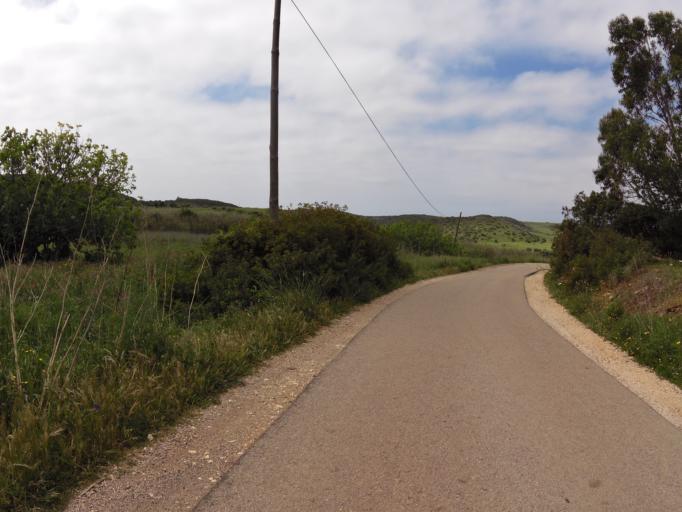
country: PT
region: Faro
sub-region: Vila do Bispo
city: Vila do Bispo
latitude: 37.0685
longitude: -8.8536
